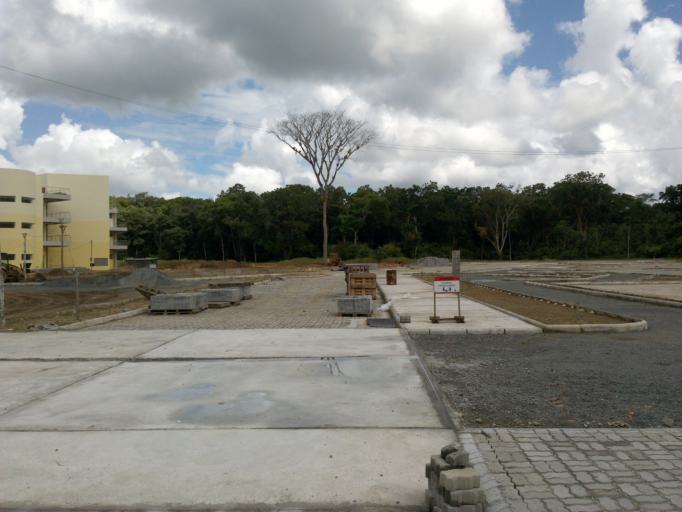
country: BR
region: Bahia
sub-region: Itabuna
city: Itabuna
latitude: -14.7711
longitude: -39.2347
